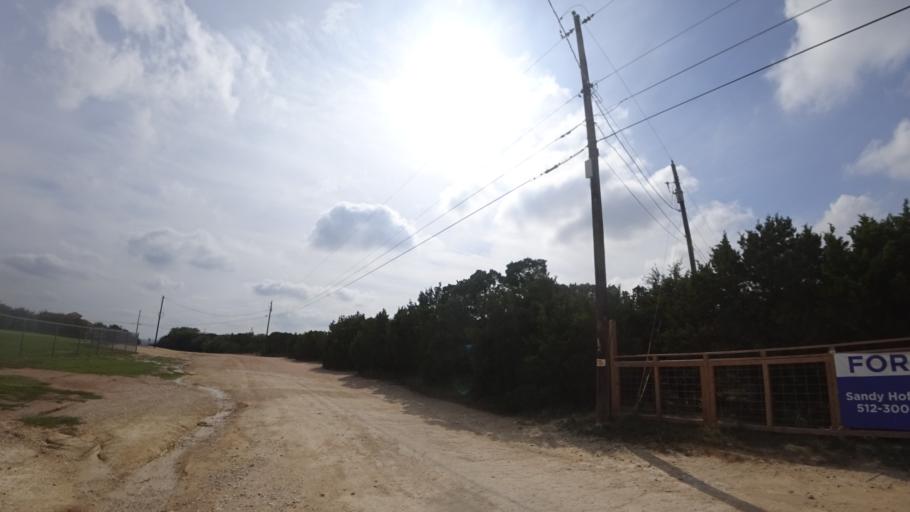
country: US
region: Texas
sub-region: Travis County
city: Hudson Bend
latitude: 30.3885
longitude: -97.9347
